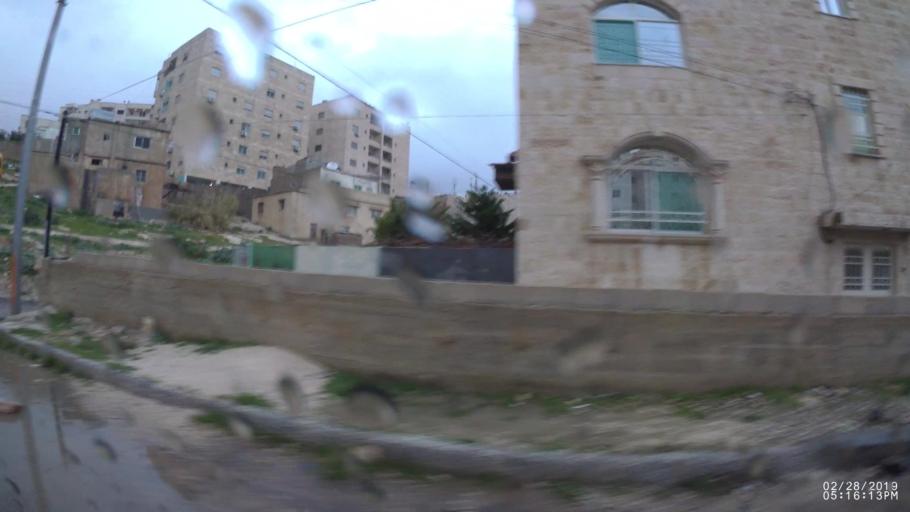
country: JO
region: Amman
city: Amman
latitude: 32.0021
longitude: 35.9233
